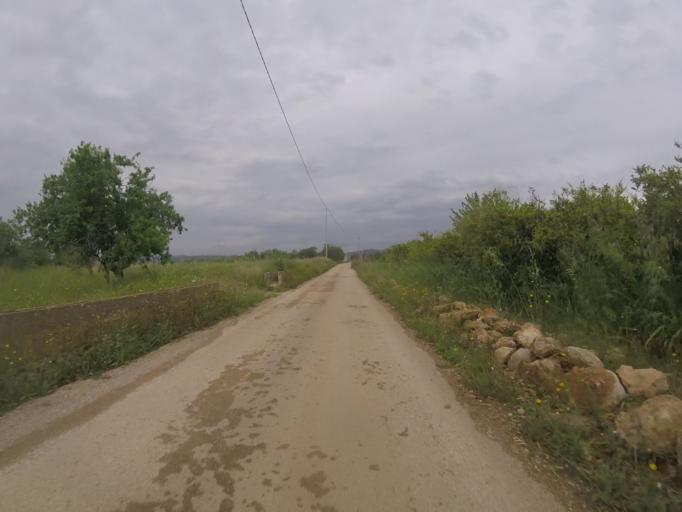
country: ES
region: Valencia
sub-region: Provincia de Castello
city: Torreblanca
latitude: 40.2176
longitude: 0.2257
